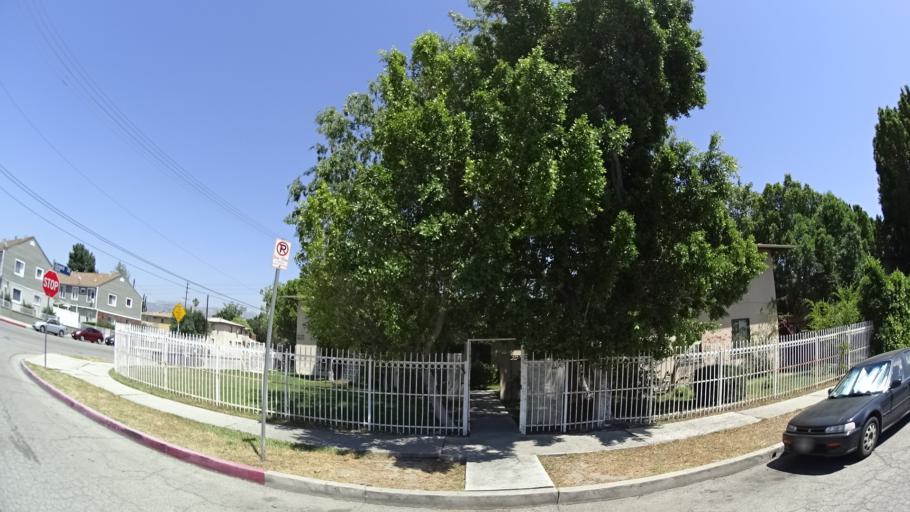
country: US
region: California
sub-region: Los Angeles County
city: North Hollywood
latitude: 34.1796
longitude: -118.3627
